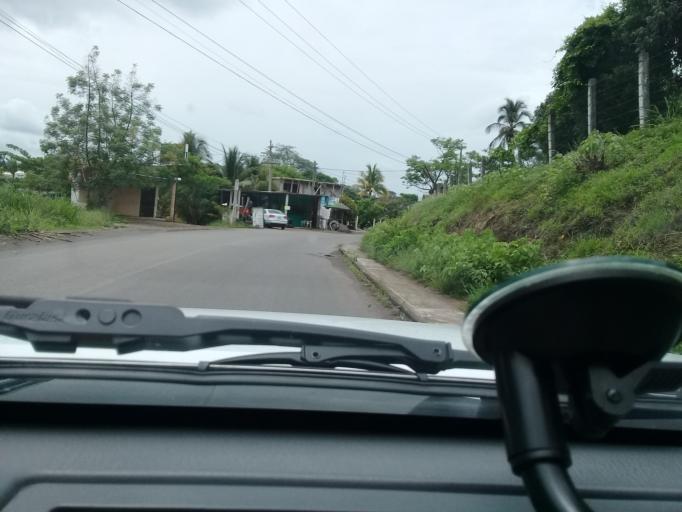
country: MX
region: Veracruz
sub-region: Paso de Ovejas
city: Tolome
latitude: 19.2710
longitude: -96.4011
